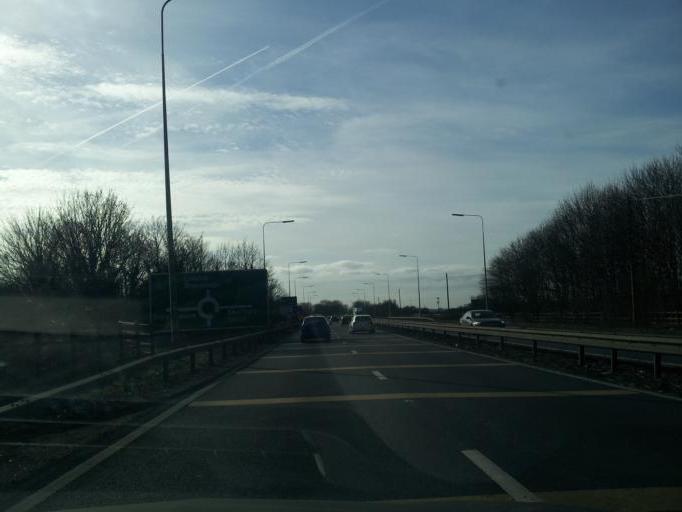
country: GB
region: England
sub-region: Central Bedfordshire
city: Biggleswade
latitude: 52.0958
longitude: -0.2747
